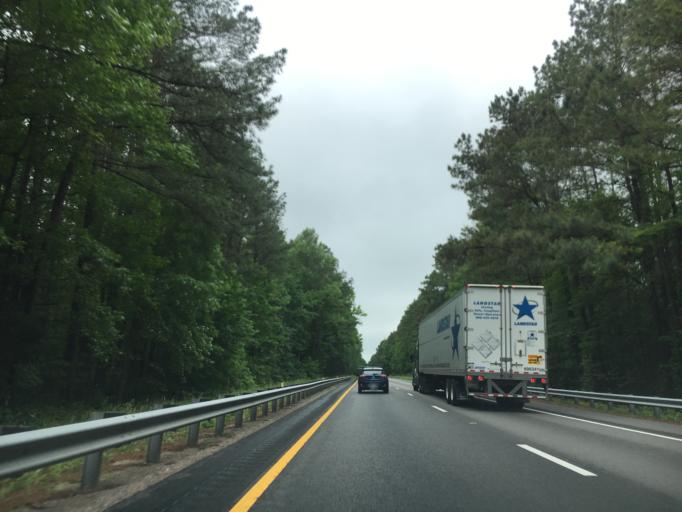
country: US
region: Virginia
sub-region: Dinwiddie County
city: Dinwiddie
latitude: 37.0601
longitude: -77.5962
